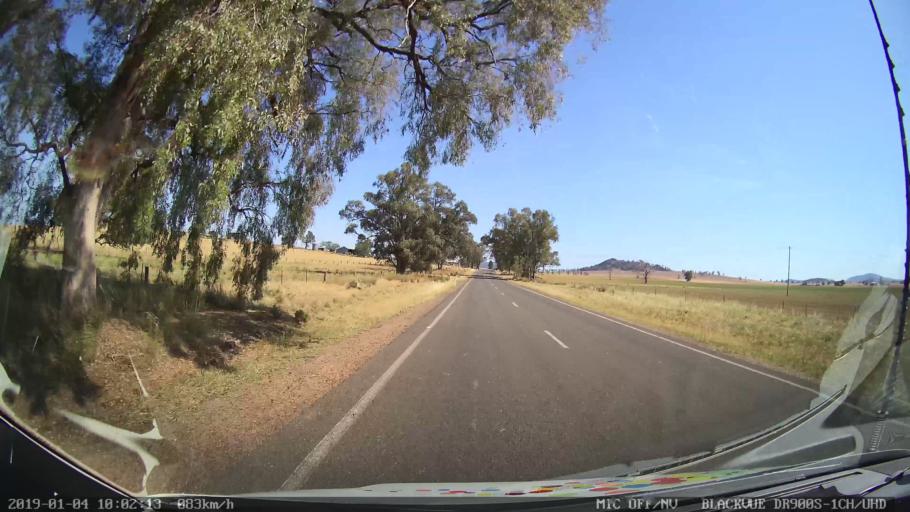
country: AU
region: New South Wales
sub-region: Cabonne
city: Canowindra
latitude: -33.4790
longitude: 148.3658
